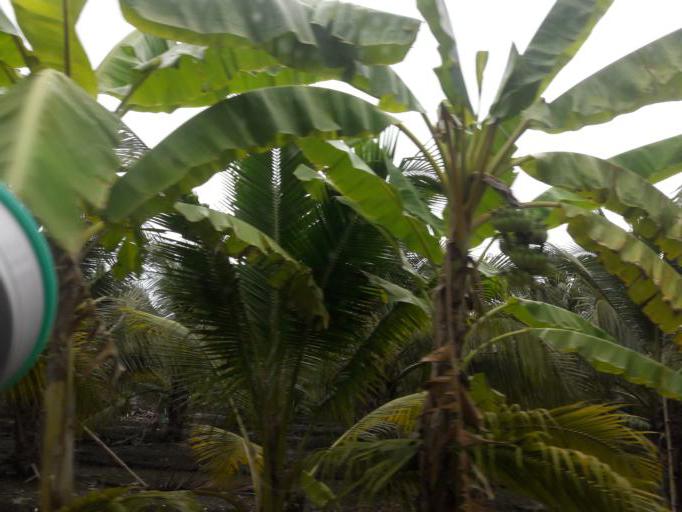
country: TH
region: Ratchaburi
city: Damnoen Saduak
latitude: 13.5087
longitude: 100.0168
